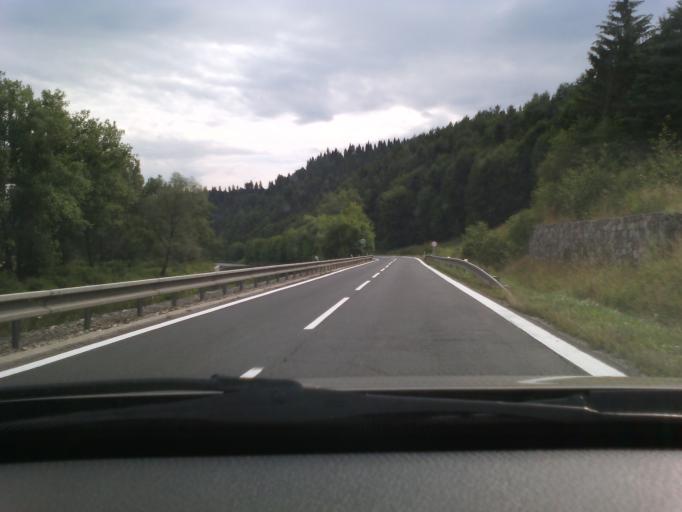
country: SK
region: Presovsky
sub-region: Okres Stara Lubovna
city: Vysne Ruzbachy
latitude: 49.2980
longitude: 20.6002
